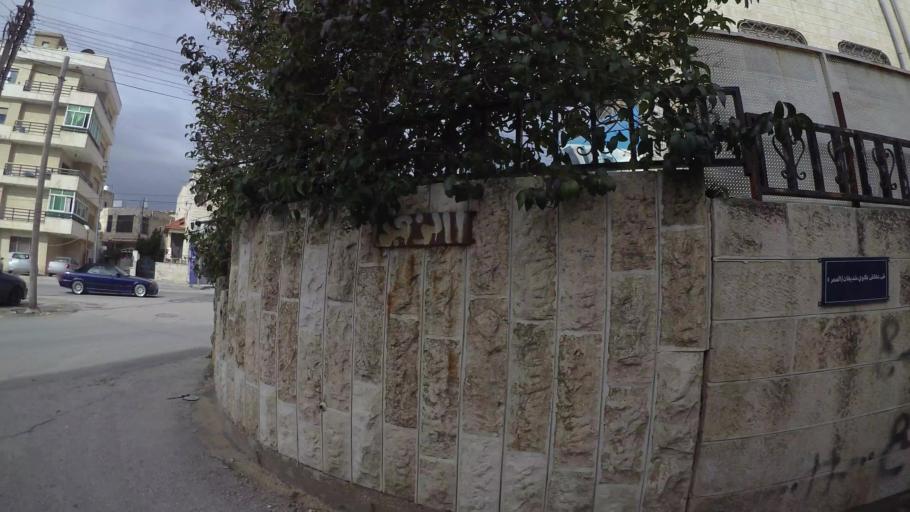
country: JO
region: Amman
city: Wadi as Sir
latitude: 31.9480
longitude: 35.8403
